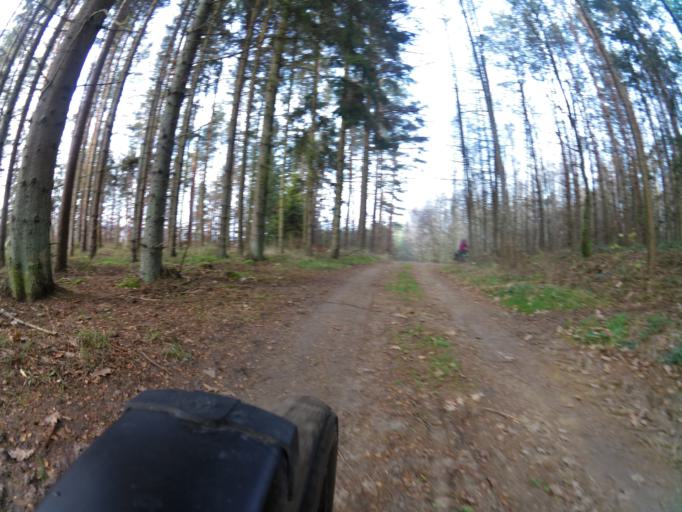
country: PL
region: West Pomeranian Voivodeship
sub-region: Powiat koszalinski
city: Polanow
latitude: 54.1990
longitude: 16.7193
